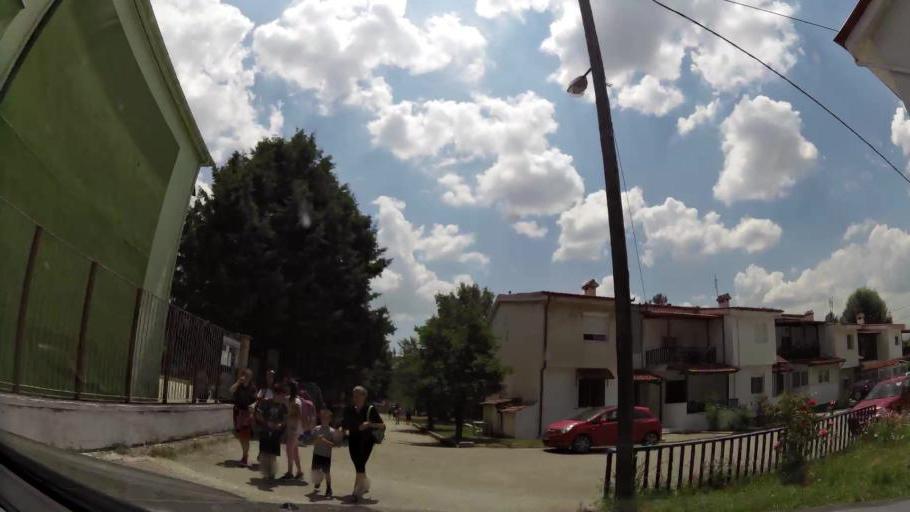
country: GR
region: West Macedonia
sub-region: Nomos Kozanis
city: Kozani
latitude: 40.2905
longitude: 21.7871
